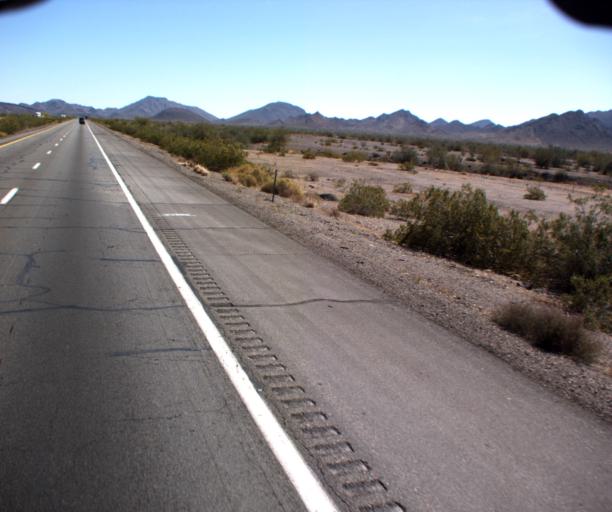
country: US
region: Arizona
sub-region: La Paz County
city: Quartzsite
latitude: 33.6742
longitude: -114.1355
